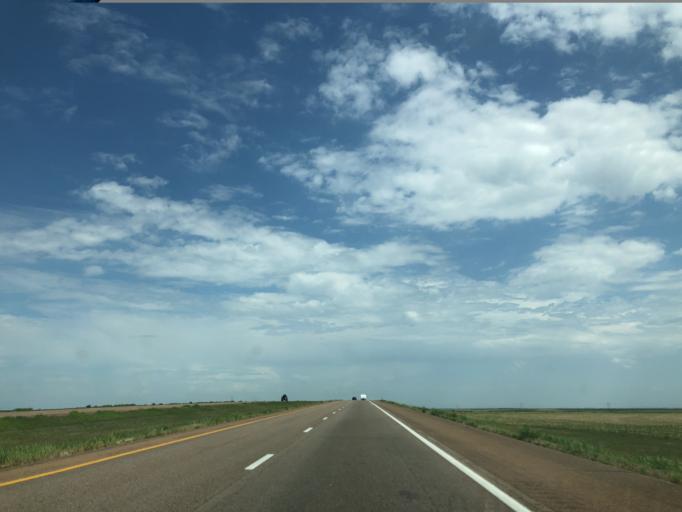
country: US
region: Kansas
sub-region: Thomas County
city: Colby
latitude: 39.3147
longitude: -100.9813
